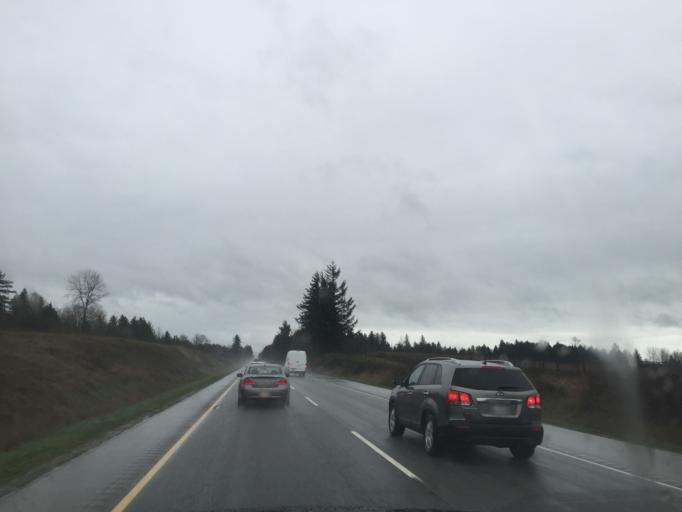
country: CA
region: British Columbia
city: Aldergrove
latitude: 49.0795
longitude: -122.4372
